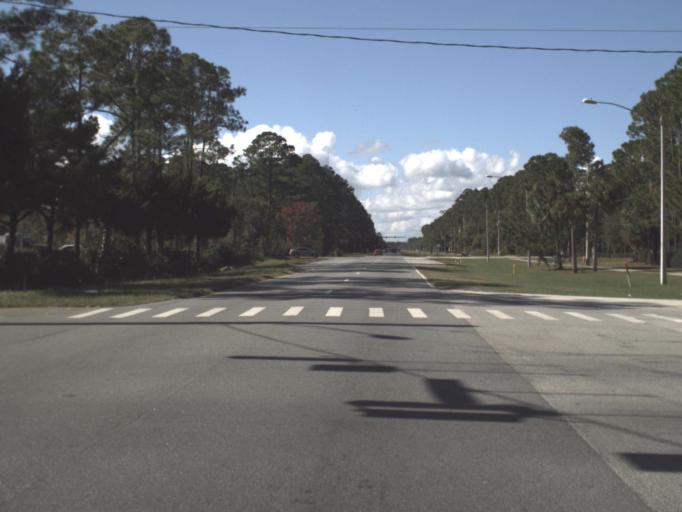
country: US
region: Florida
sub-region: Flagler County
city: Palm Coast
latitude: 29.5534
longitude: -81.2371
